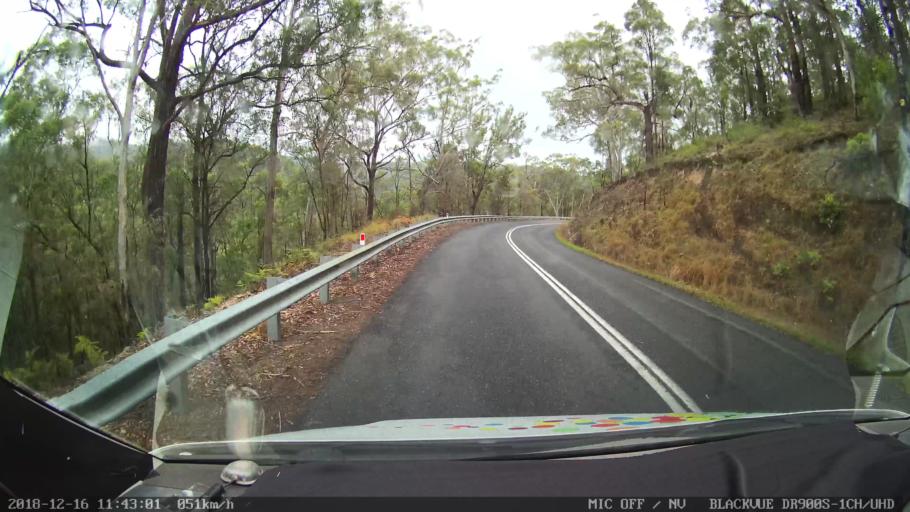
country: AU
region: New South Wales
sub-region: Tenterfield Municipality
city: Carrolls Creek
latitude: -28.9486
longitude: 152.2153
